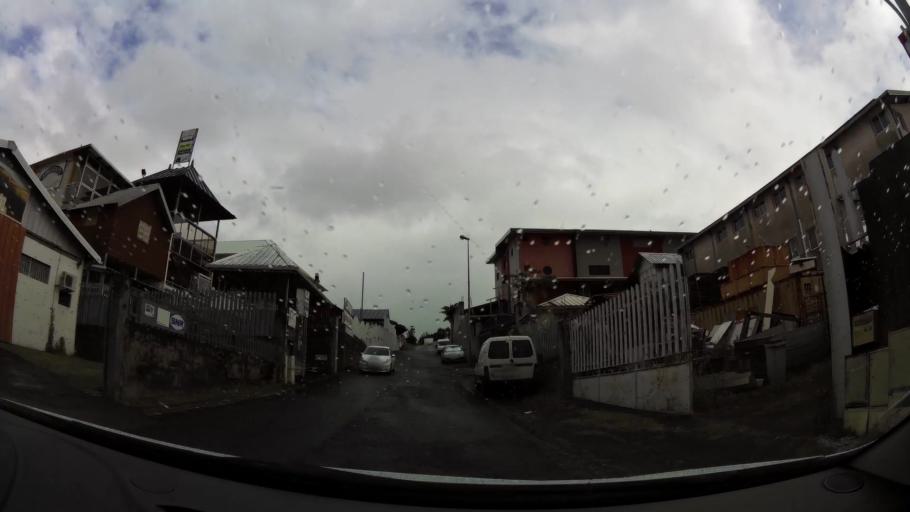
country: RE
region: Reunion
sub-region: Reunion
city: Saint-Andre
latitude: -20.9316
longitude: 55.6377
